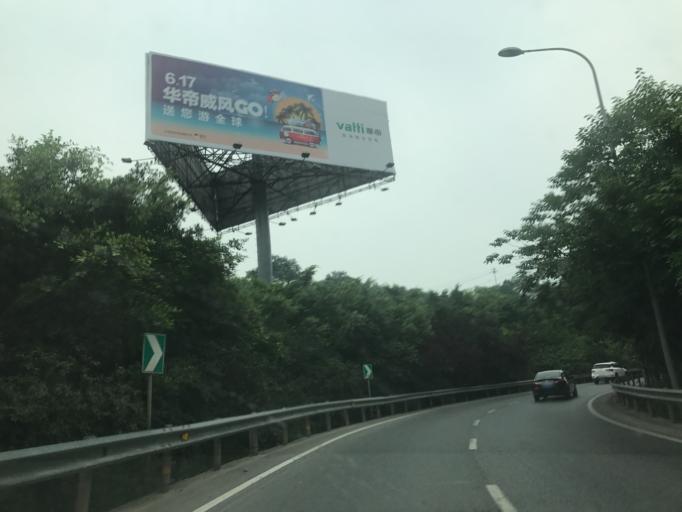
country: CN
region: Chongqing Shi
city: Cuntan
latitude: 29.6130
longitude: 106.5586
